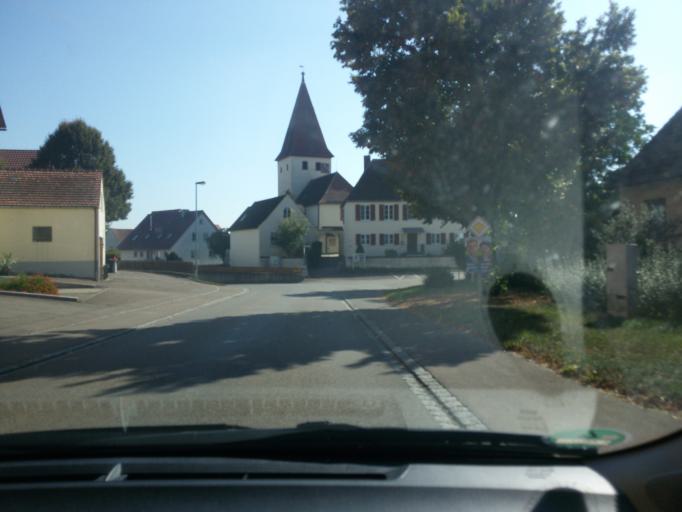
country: DE
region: Bavaria
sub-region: Swabia
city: Hainsfarth
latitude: 48.9822
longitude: 10.6113
